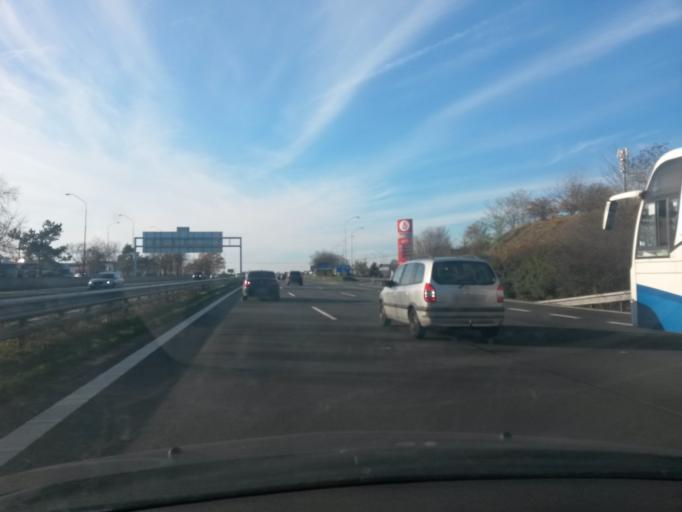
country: CZ
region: Central Bohemia
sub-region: Okres Praha-Zapad
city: Pruhonice
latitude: 50.0092
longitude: 14.5453
